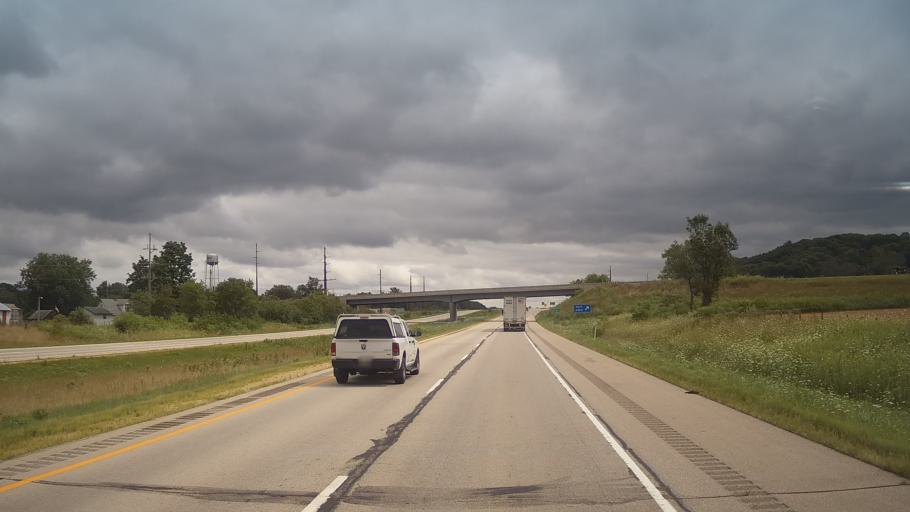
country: US
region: Wisconsin
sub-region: La Crosse County
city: Bangor
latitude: 43.8981
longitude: -90.9219
